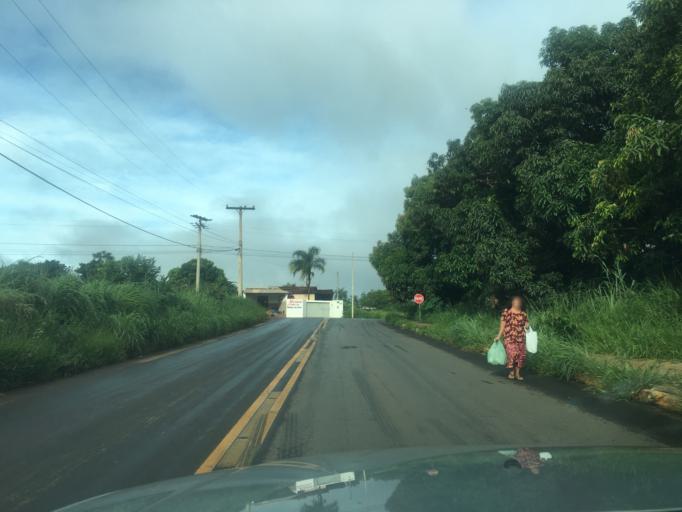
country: BR
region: Goias
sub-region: Aparecida De Goiania
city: Aparecida de Goiania
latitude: -16.8034
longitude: -49.2476
